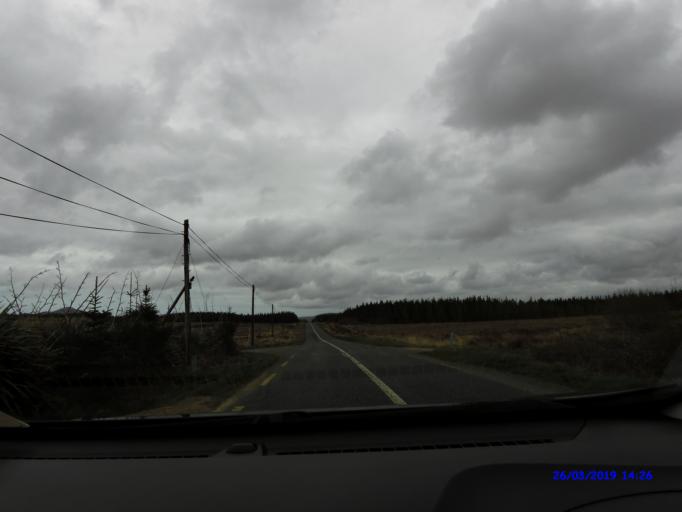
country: IE
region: Connaught
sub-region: Maigh Eo
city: Belmullet
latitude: 54.2440
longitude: -9.6452
